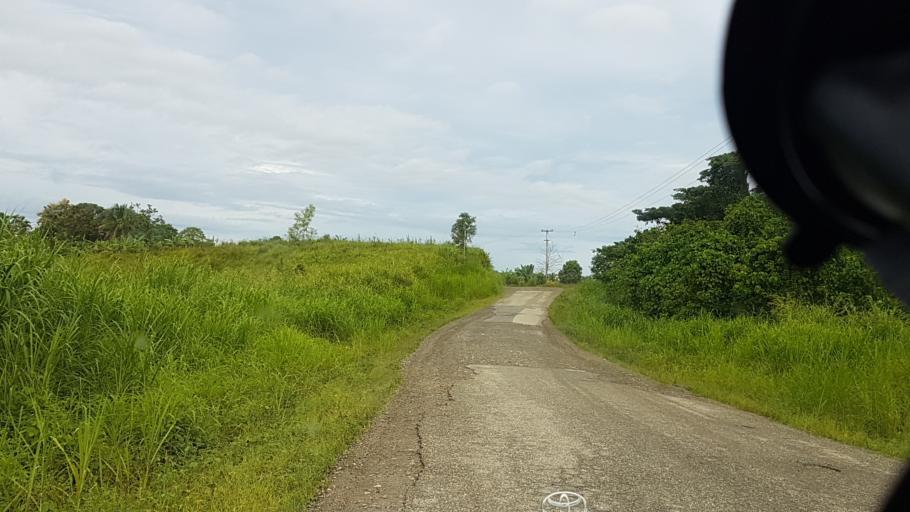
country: PG
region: East Sepik
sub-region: Wewak
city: Wewak
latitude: -3.6992
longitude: 143.2450
